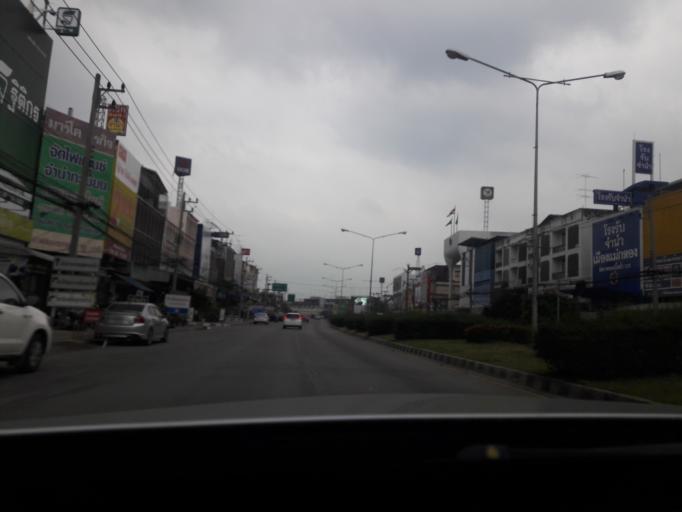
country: TH
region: Samut Songkhram
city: Samut Songkhram
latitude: 13.4044
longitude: 100.0019
